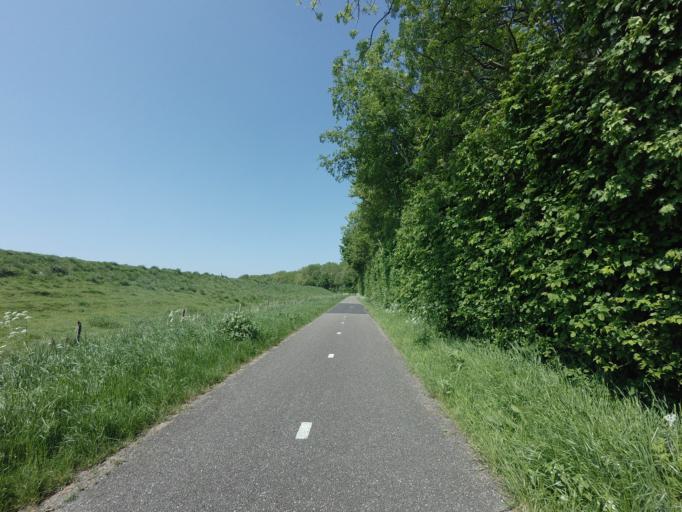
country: NL
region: Zeeland
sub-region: Gemeente Veere
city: Veere
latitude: 51.5284
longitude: 3.6816
